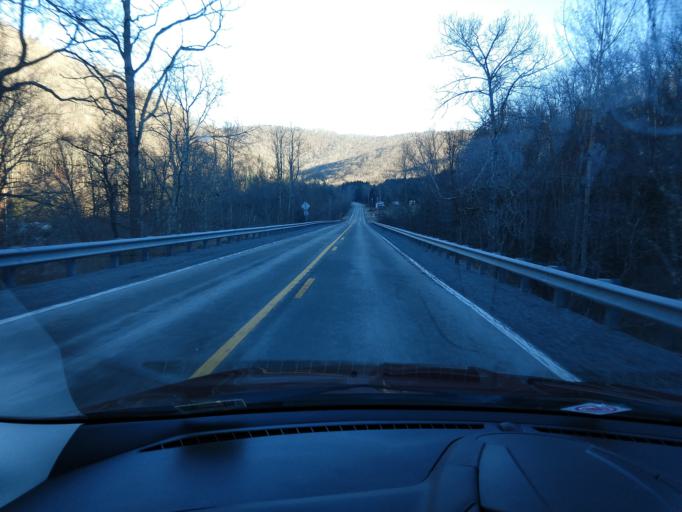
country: US
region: Virginia
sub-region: Highland County
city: Monterey
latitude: 38.5000
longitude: -79.7128
